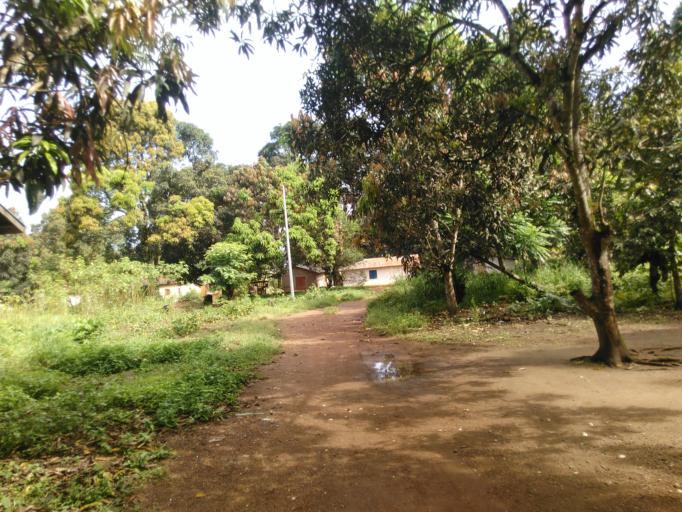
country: SL
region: Southern Province
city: Rotifunk
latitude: 8.4860
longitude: -12.7599
